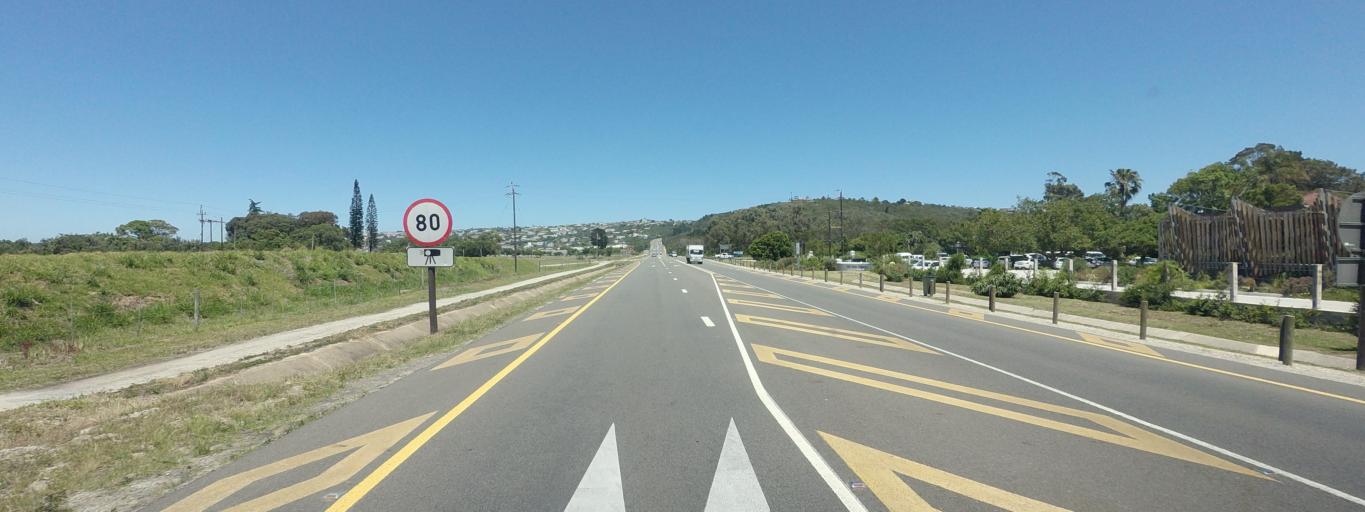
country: ZA
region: Western Cape
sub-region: Eden District Municipality
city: Plettenberg Bay
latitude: -34.0344
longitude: 23.3738
